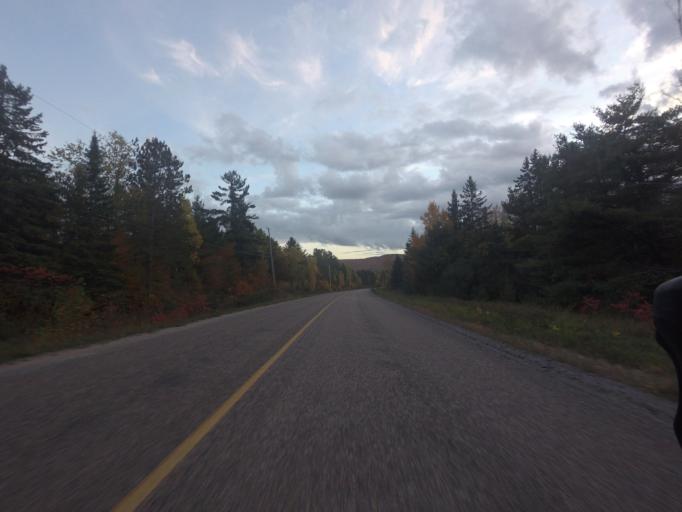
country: CA
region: Ontario
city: Renfrew
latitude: 45.3793
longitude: -76.9577
